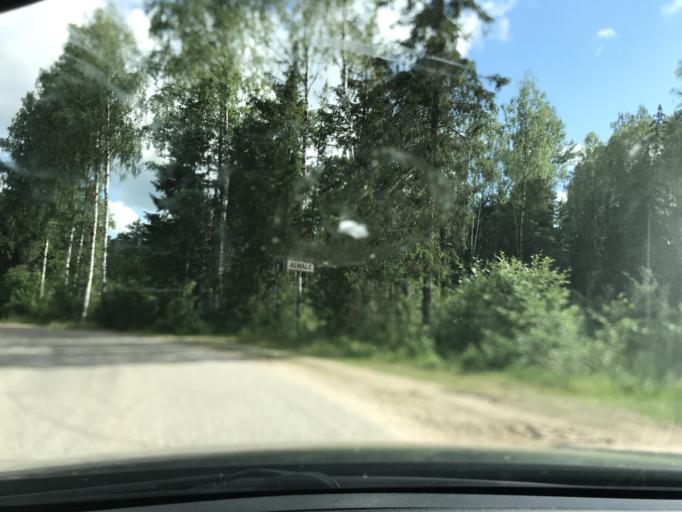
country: LV
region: Alsunga
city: Alsunga
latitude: 56.9846
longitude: 21.6298
